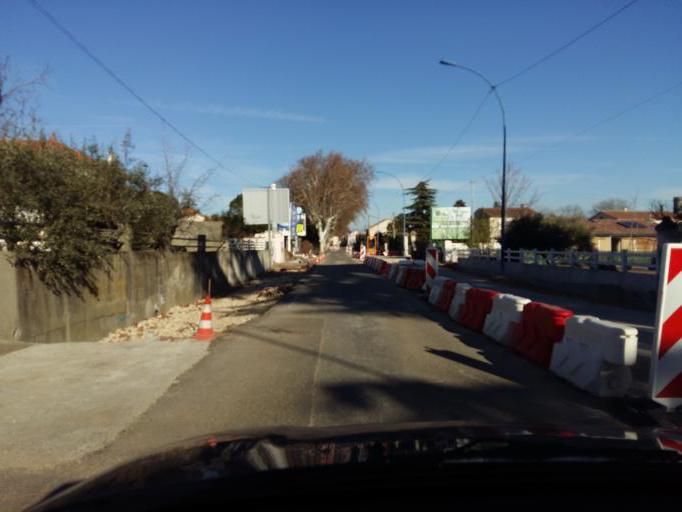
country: FR
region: Languedoc-Roussillon
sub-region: Departement du Gard
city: Pont-Saint-Esprit
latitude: 44.2463
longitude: 4.6438
